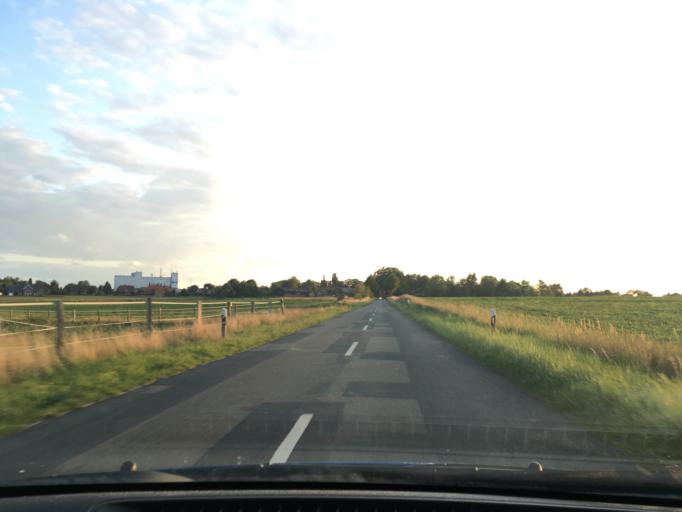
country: DE
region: Lower Saxony
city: Tosterglope
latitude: 53.2476
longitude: 10.7913
